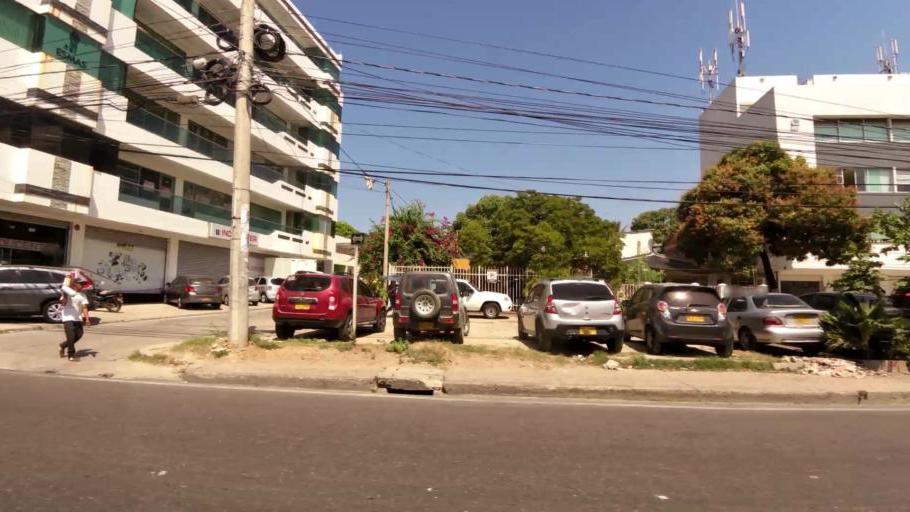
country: CO
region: Bolivar
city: Cartagena
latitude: 10.3873
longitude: -75.5104
